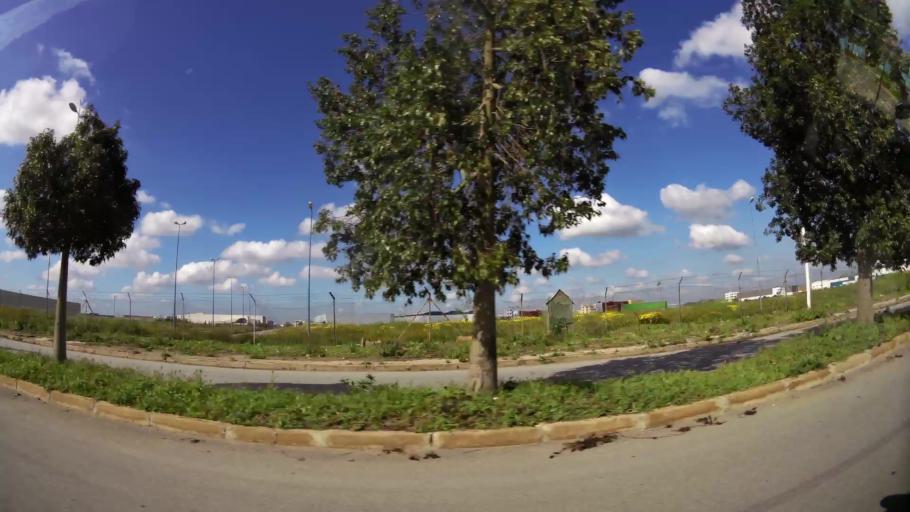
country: MA
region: Grand Casablanca
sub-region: Mediouna
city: Mediouna
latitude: 33.3903
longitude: -7.5428
